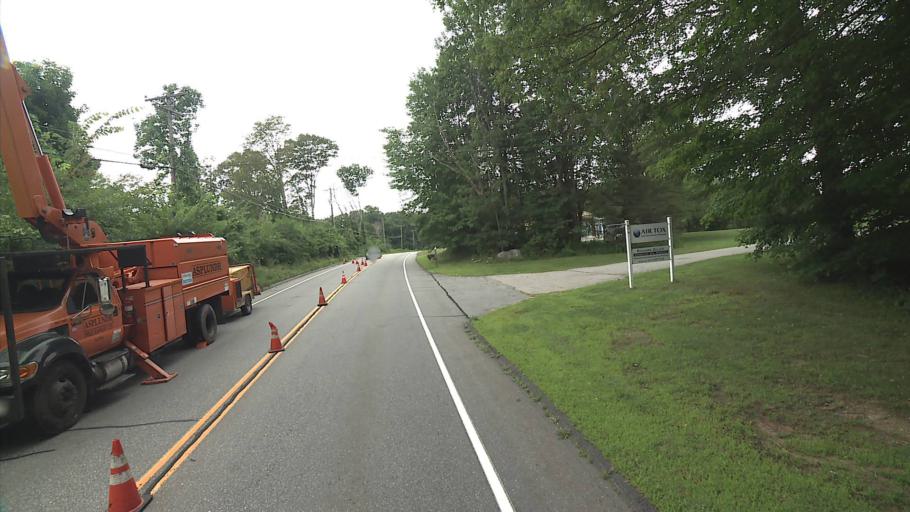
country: US
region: Connecticut
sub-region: Tolland County
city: Storrs
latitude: 41.8728
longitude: -72.2207
